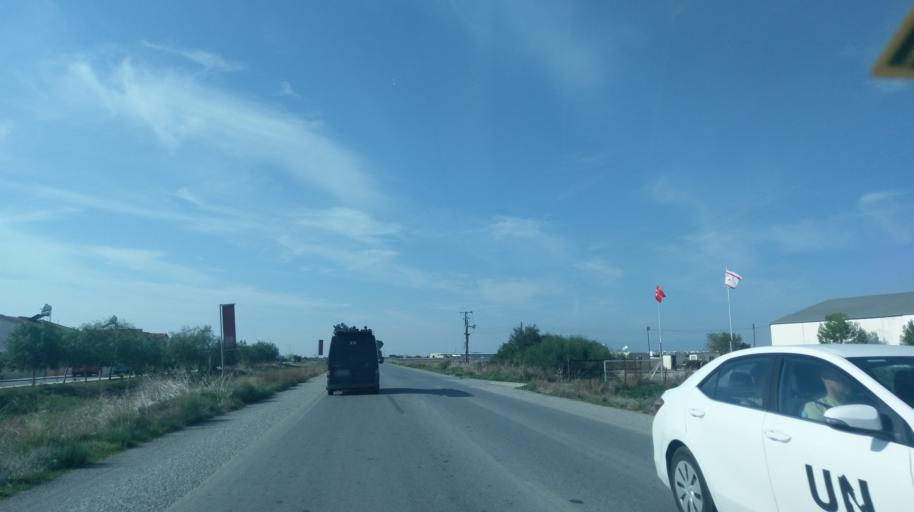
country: CY
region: Ammochostos
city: Acheritou
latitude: 35.1521
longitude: 33.8588
